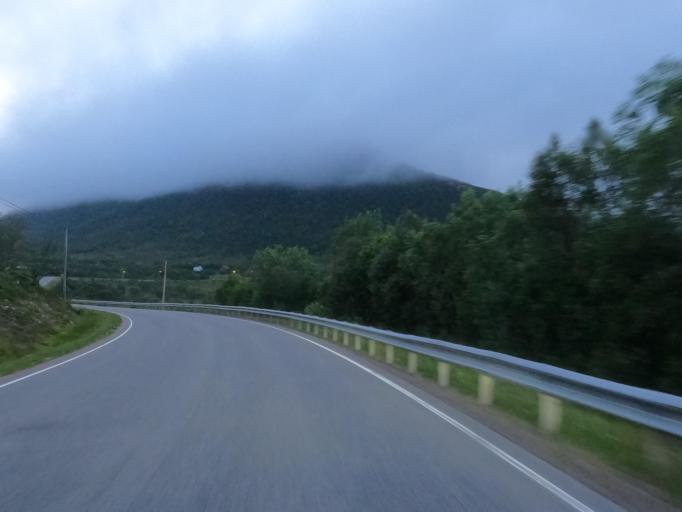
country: NO
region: Nordland
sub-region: Lodingen
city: Lodingen
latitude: 68.6133
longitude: 15.7727
